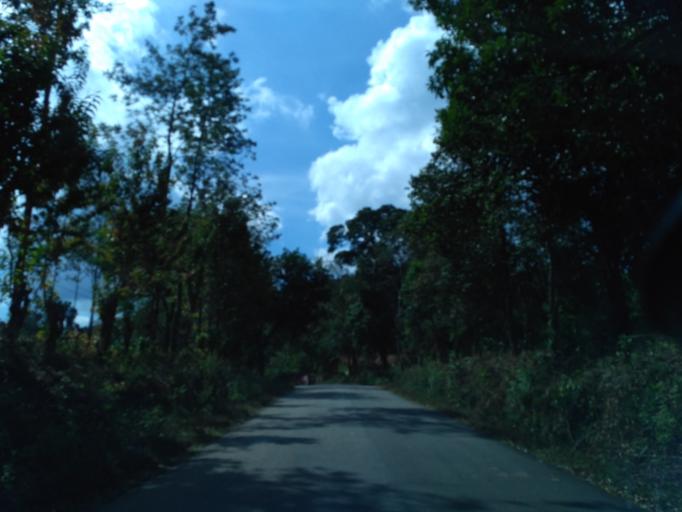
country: IN
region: Karnataka
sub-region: Kodagu
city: Madikeri
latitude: 12.3775
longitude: 75.5716
